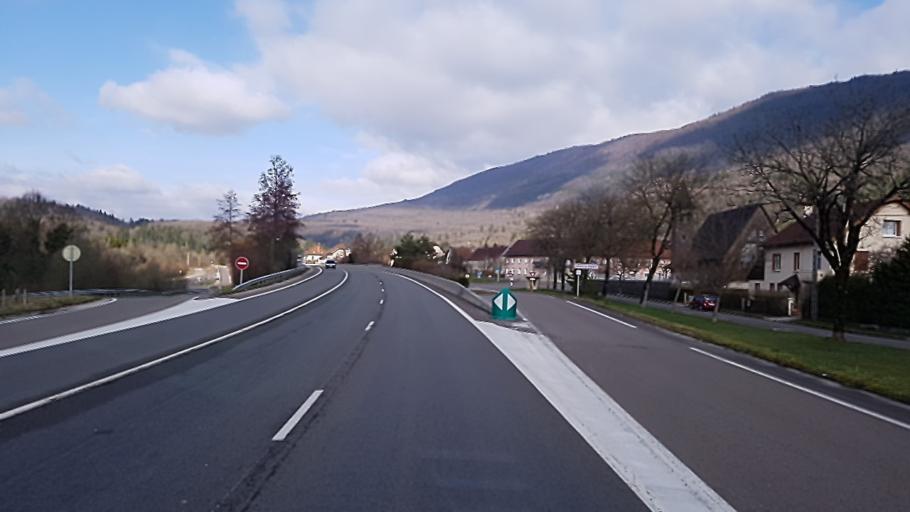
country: FR
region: Rhone-Alpes
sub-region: Departement de l'Ain
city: Dortan
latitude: 46.3300
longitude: 5.6771
